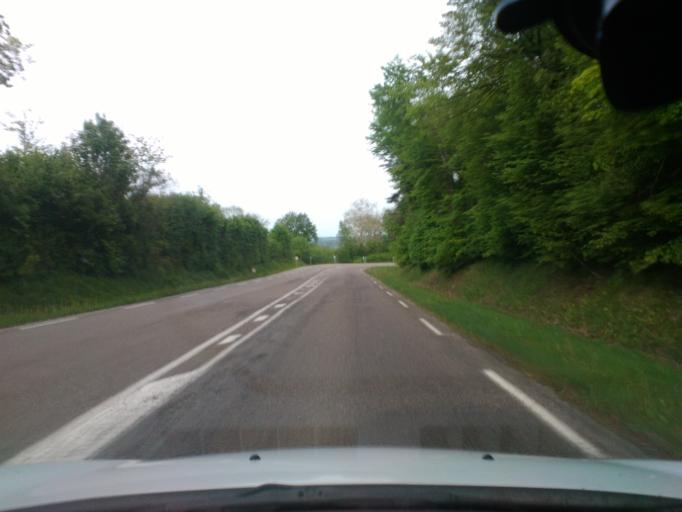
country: FR
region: Champagne-Ardenne
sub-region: Departement de la Haute-Marne
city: Chaumont
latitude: 48.1407
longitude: 5.0482
